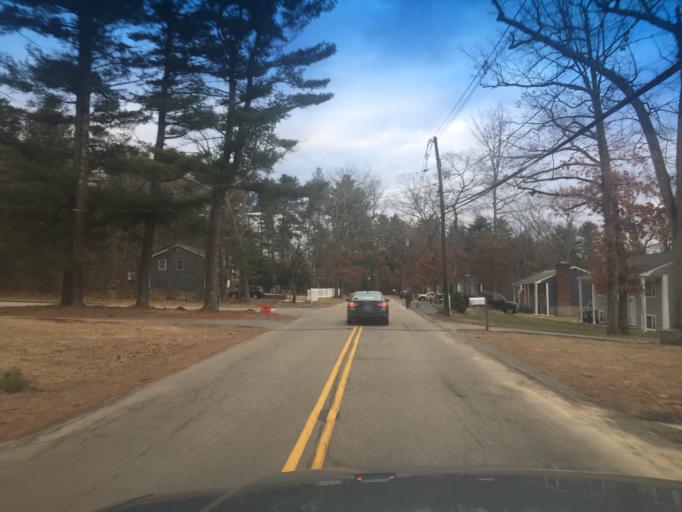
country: US
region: Massachusetts
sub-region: Norfolk County
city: Medway
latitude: 42.1501
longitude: -71.3816
